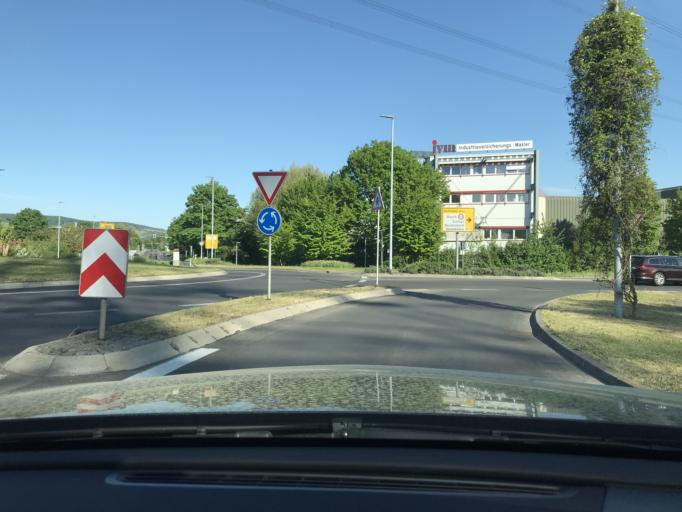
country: DE
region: Baden-Wuerttemberg
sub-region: Regierungsbezirk Stuttgart
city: Weinstadt-Endersbach
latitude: 48.8129
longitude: 9.3796
